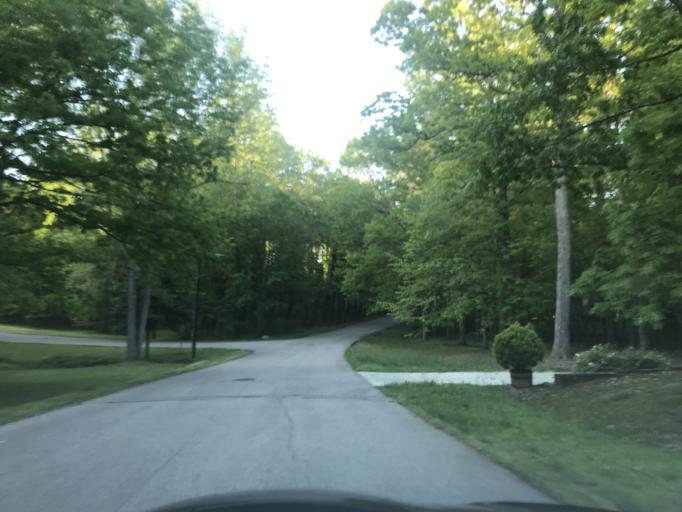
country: US
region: North Carolina
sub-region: Wake County
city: Wake Forest
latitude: 35.8990
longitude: -78.6038
